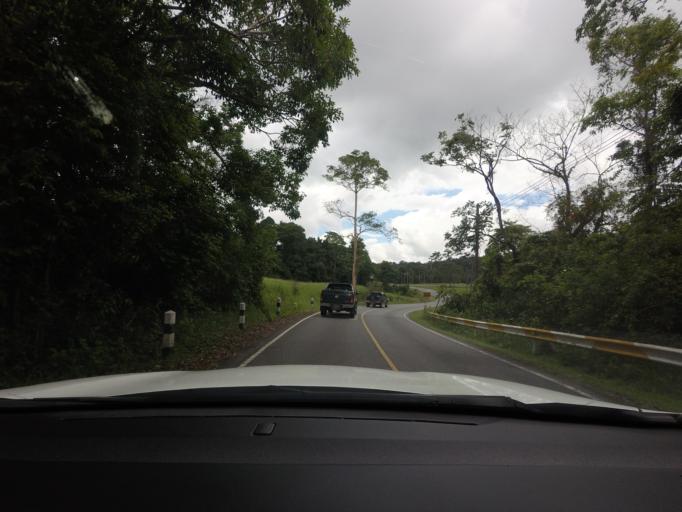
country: TH
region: Nakhon Ratchasima
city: Pak Chong
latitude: 14.4493
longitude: 101.3683
